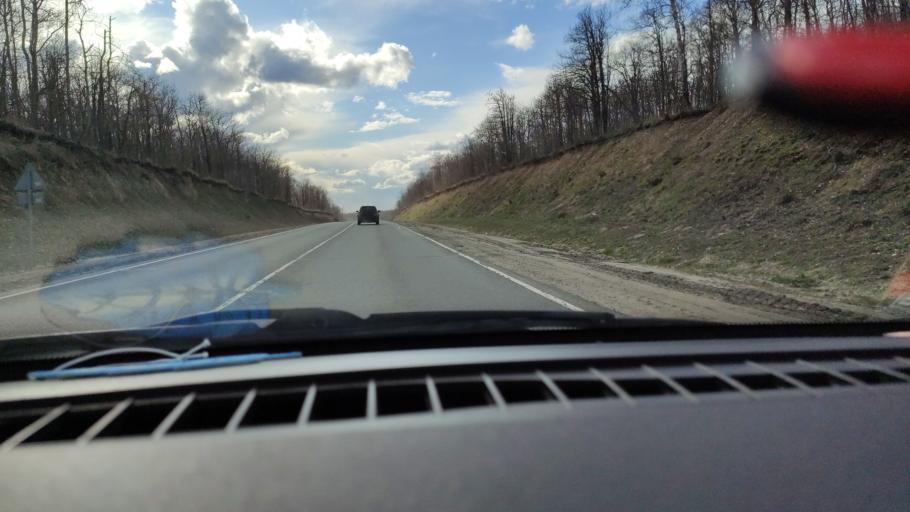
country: RU
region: Saratov
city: Vol'sk
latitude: 52.1082
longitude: 47.3940
